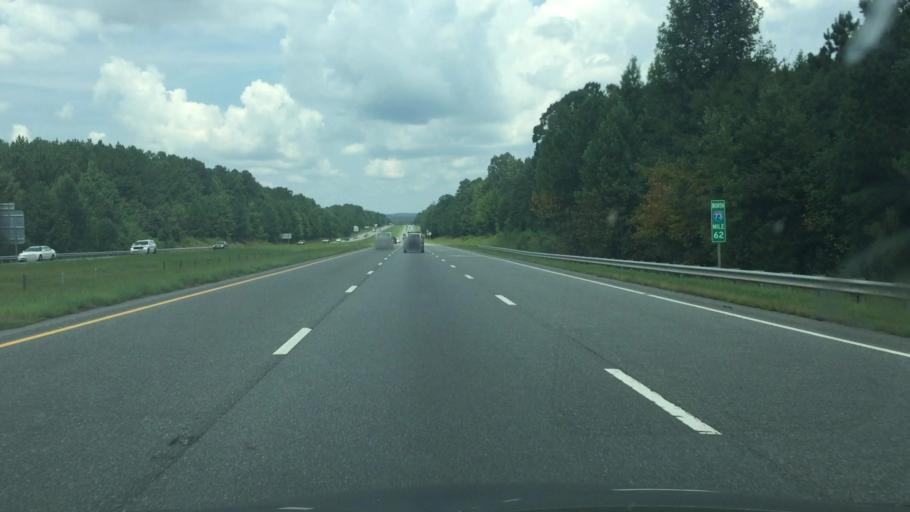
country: US
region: North Carolina
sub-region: Randolph County
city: Asheboro
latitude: 35.5399
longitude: -79.7925
